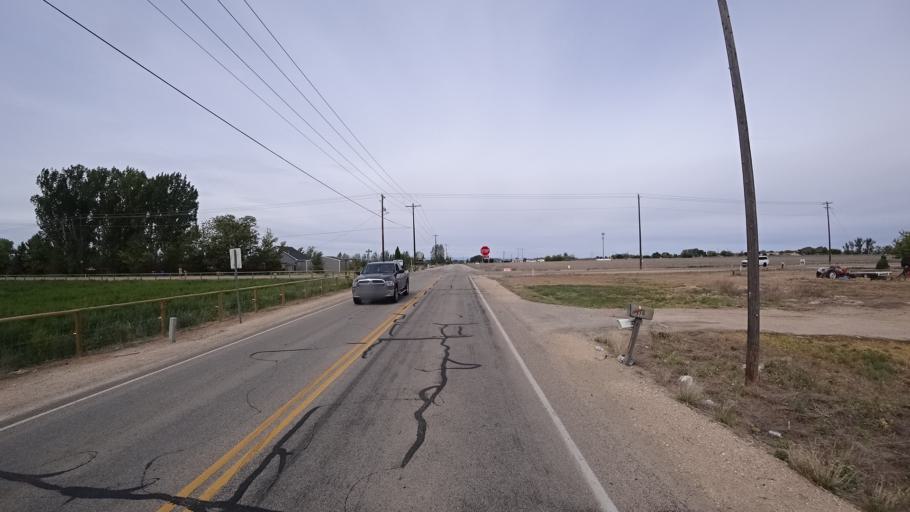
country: US
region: Idaho
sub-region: Ada County
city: Meridian
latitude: 43.5611
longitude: -116.4332
